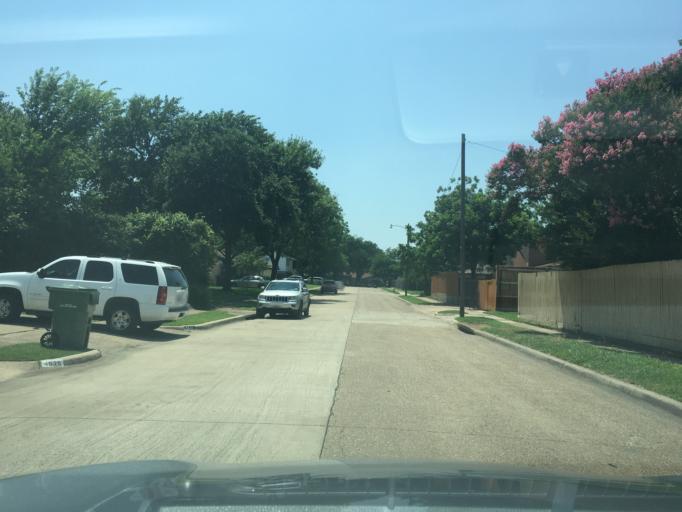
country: US
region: Texas
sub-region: Dallas County
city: Richardson
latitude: 32.9192
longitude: -96.7034
